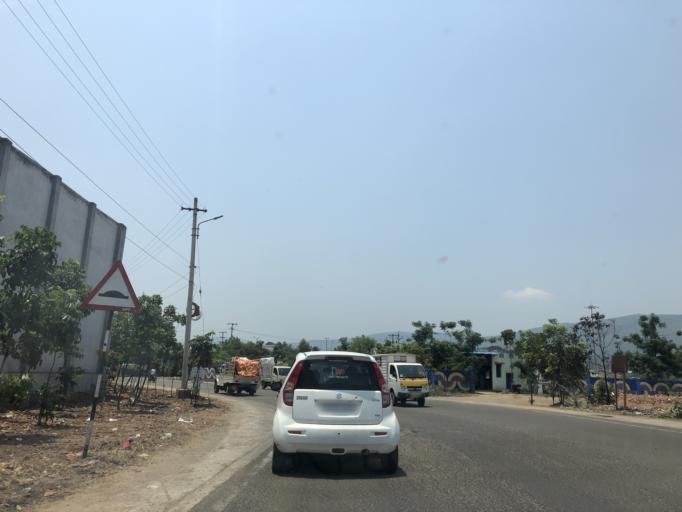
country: IN
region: Andhra Pradesh
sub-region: Vishakhapatnam
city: Yarada
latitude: 17.7165
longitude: 83.2914
